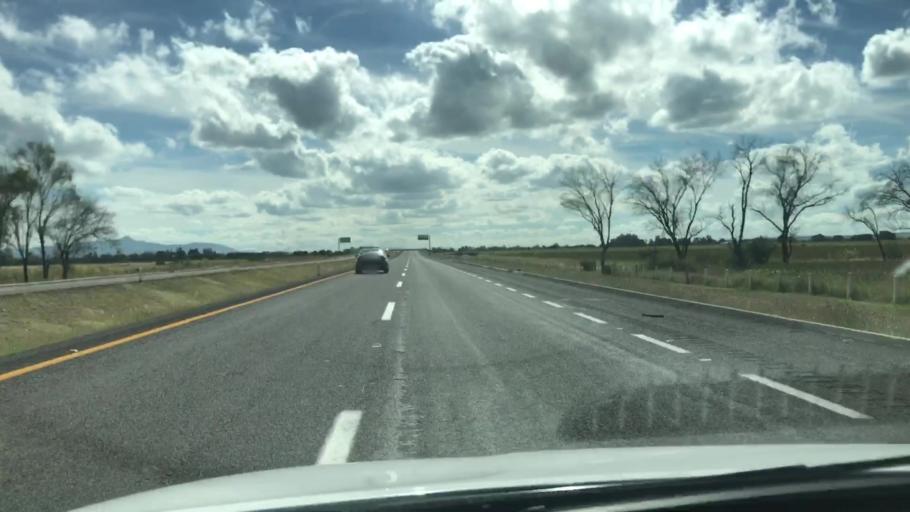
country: MX
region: Guanajuato
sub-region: Leon
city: San Antonio de los Tepetates
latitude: 21.0200
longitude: -101.6086
